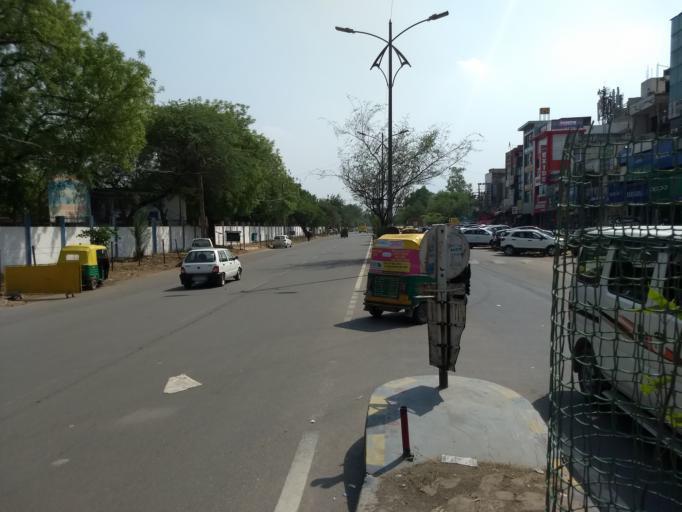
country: IN
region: Haryana
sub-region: Gurgaon
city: Gurgaon
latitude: 28.4747
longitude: 77.0430
